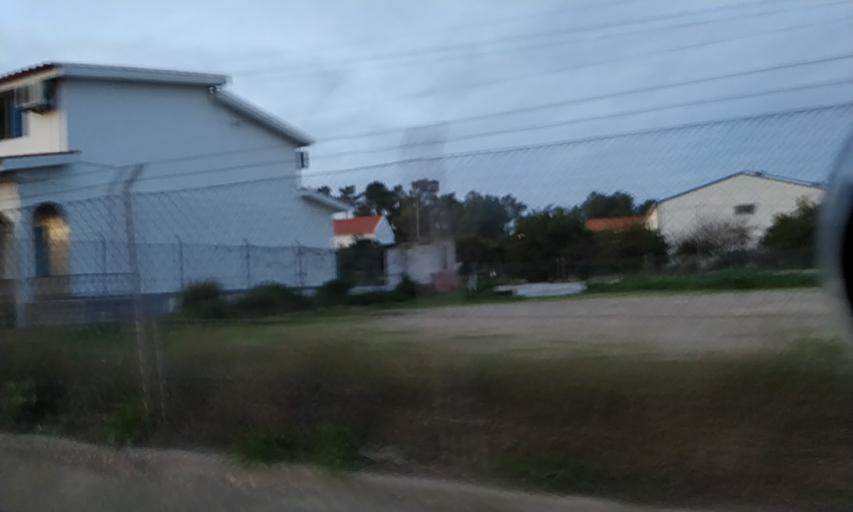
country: PT
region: Setubal
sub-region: Setubal
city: Setubal
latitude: 38.5236
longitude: -8.8358
